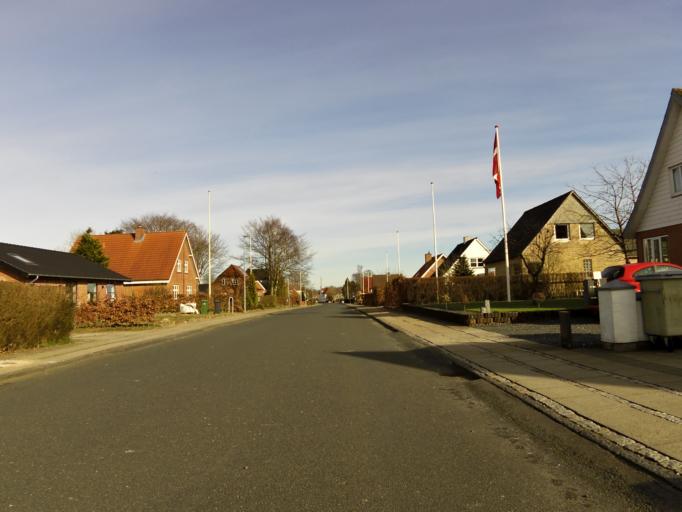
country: DK
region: South Denmark
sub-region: Kolding Kommune
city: Vamdrup
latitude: 55.3567
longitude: 9.1924
